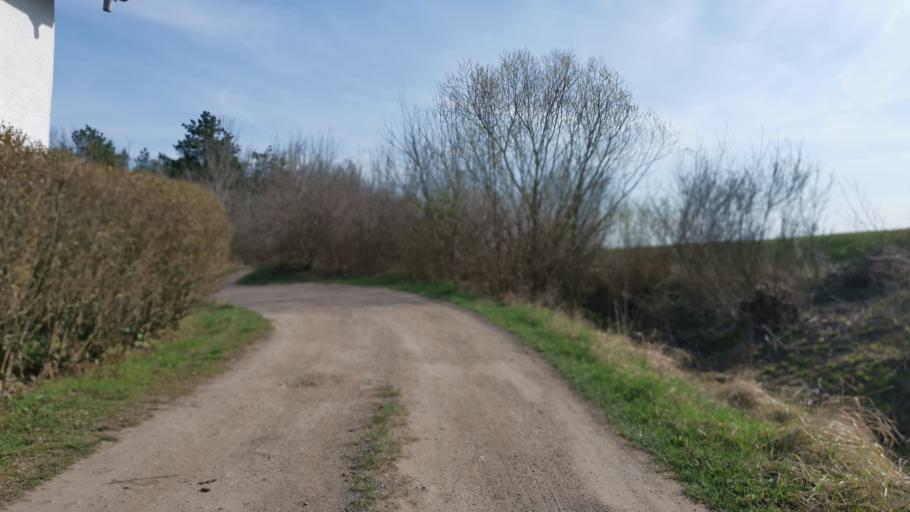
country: CZ
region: South Moravian
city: Tvrdonice
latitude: 48.7188
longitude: 17.0224
